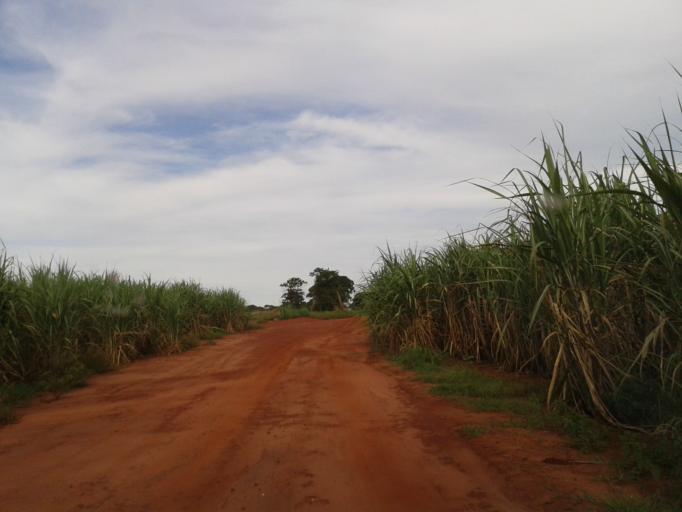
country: BR
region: Minas Gerais
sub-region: Capinopolis
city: Capinopolis
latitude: -18.7943
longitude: -49.8215
